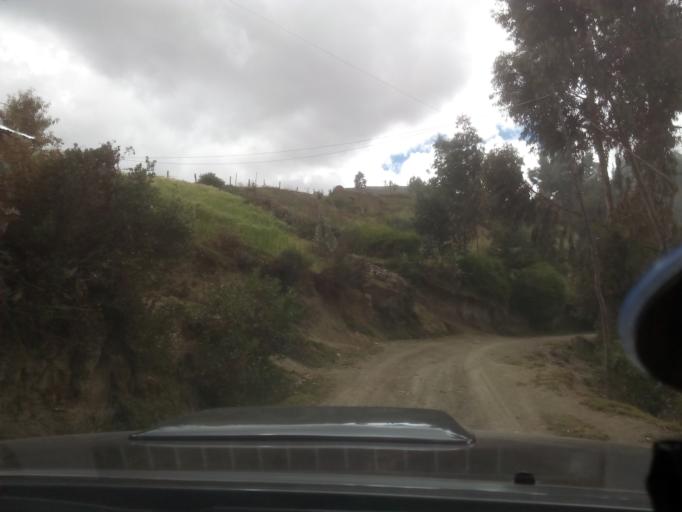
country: PE
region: Ayacucho
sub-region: Provincia de Huanta
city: Luricocha
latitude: -12.8821
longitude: -74.2181
